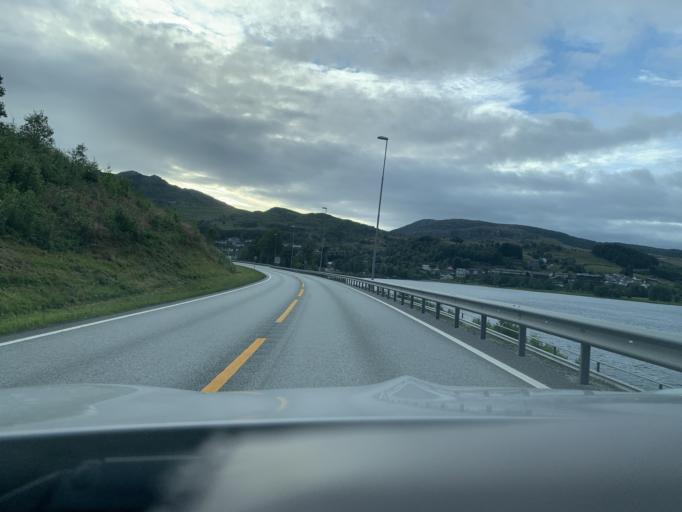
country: NO
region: Rogaland
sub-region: Bjerkreim
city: Vikesa
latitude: 58.6277
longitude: 6.0885
